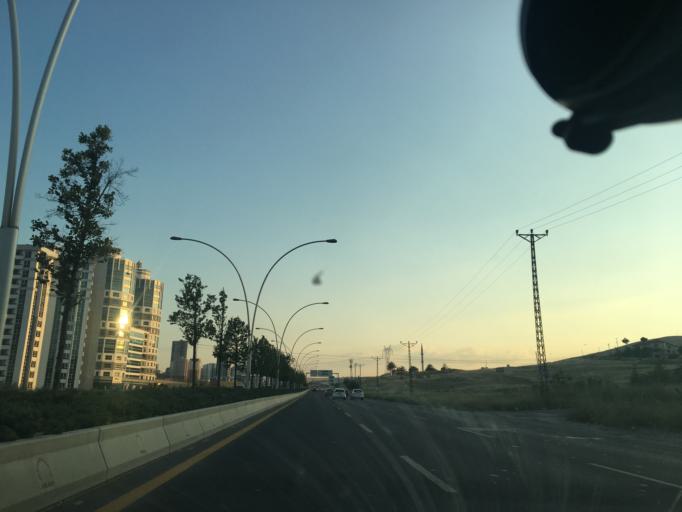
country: TR
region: Ankara
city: Etimesgut
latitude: 39.8747
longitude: 32.6489
